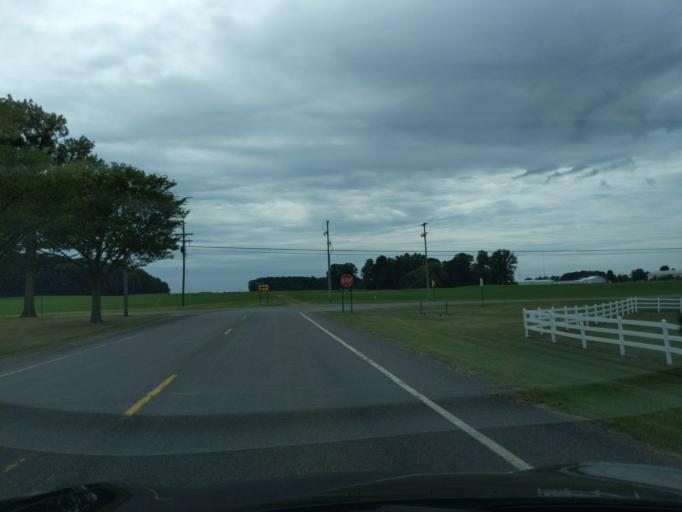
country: US
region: Michigan
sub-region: Ingham County
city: East Lansing
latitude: 42.7051
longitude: -84.4784
